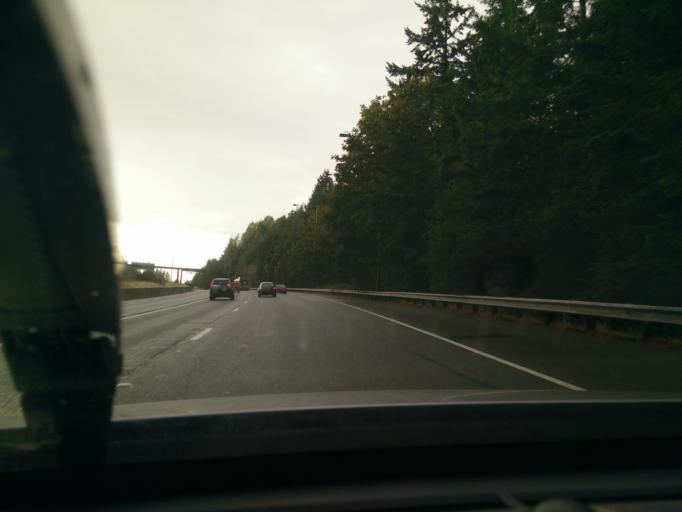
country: US
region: Washington
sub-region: Snohomish County
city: Martha Lake
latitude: 47.8207
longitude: -122.2430
